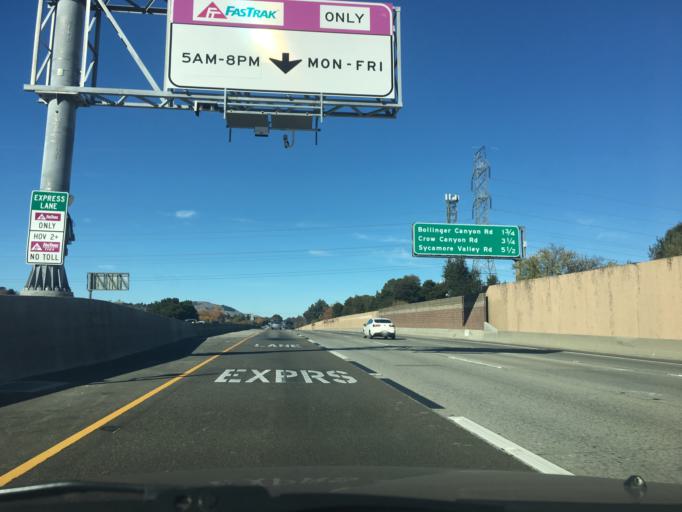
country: US
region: California
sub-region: Alameda County
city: Dublin
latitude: 37.7362
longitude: -121.9499
